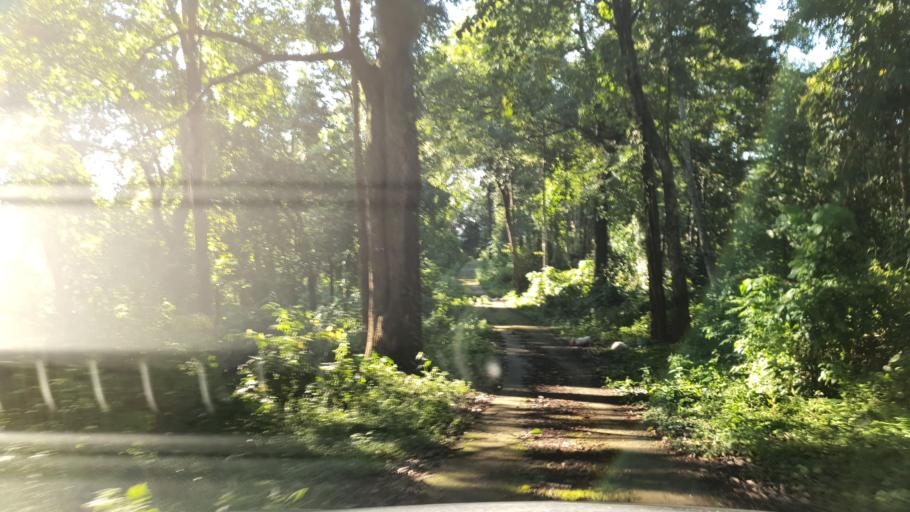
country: TH
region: Chiang Mai
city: Mae On
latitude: 18.8136
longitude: 99.3539
